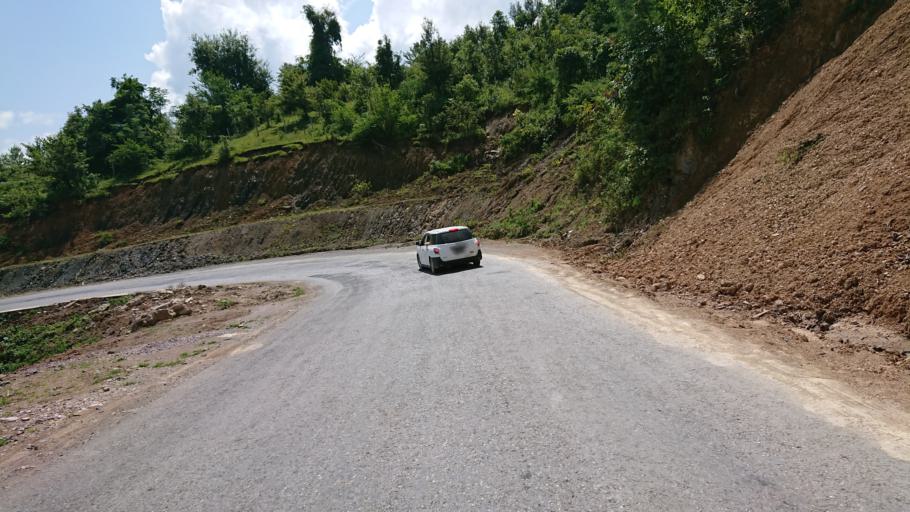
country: MM
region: Shan
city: Taunggyi
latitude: 20.8166
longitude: 97.3105
